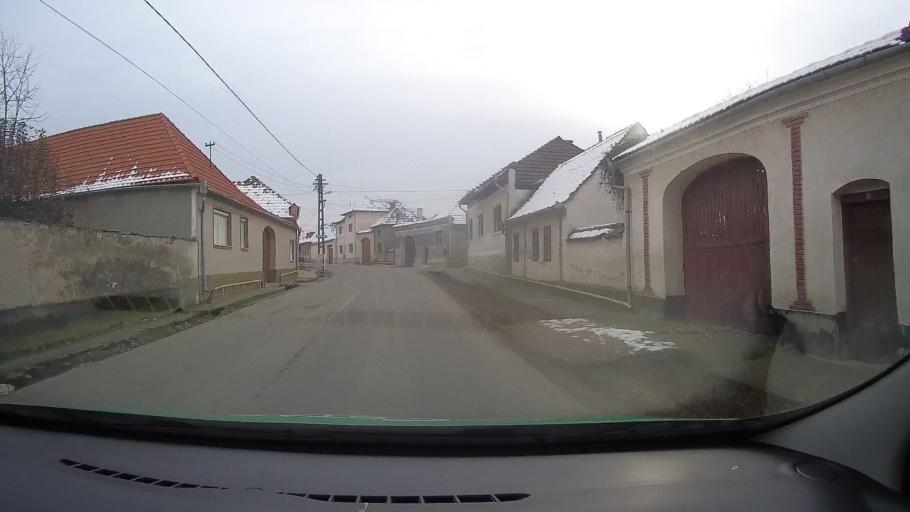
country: RO
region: Hunedoara
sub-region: Comuna Romos
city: Romos
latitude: 45.8436
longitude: 23.2739
